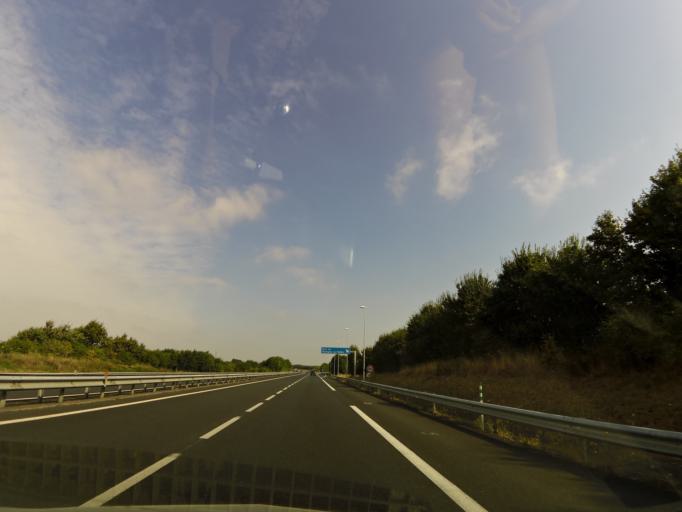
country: FR
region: Pays de la Loire
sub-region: Departement de la Vendee
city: Chauche
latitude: 46.8676
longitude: -1.2844
